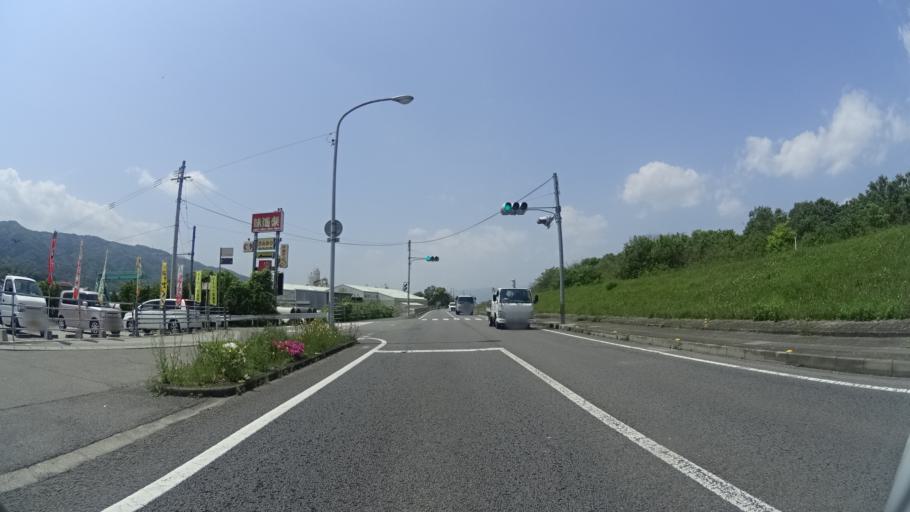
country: JP
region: Tokushima
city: Kamojimacho-jogejima
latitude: 34.0612
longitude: 134.2964
